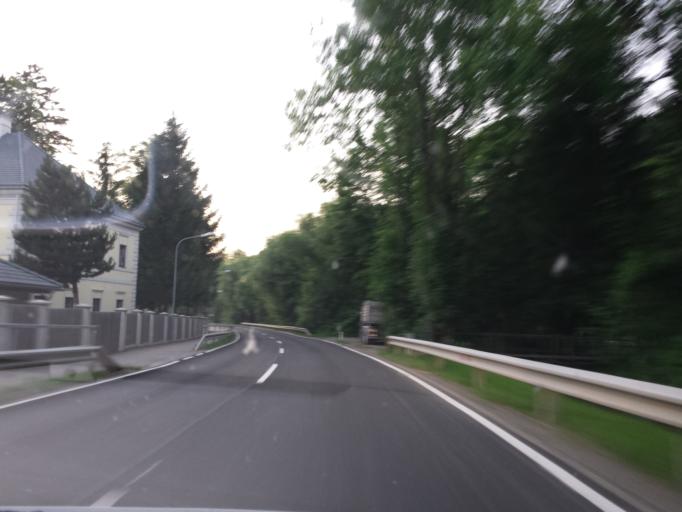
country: AT
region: Lower Austria
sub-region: Politischer Bezirk Lilienfeld
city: Hainfeld
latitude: 48.0248
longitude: 15.7759
